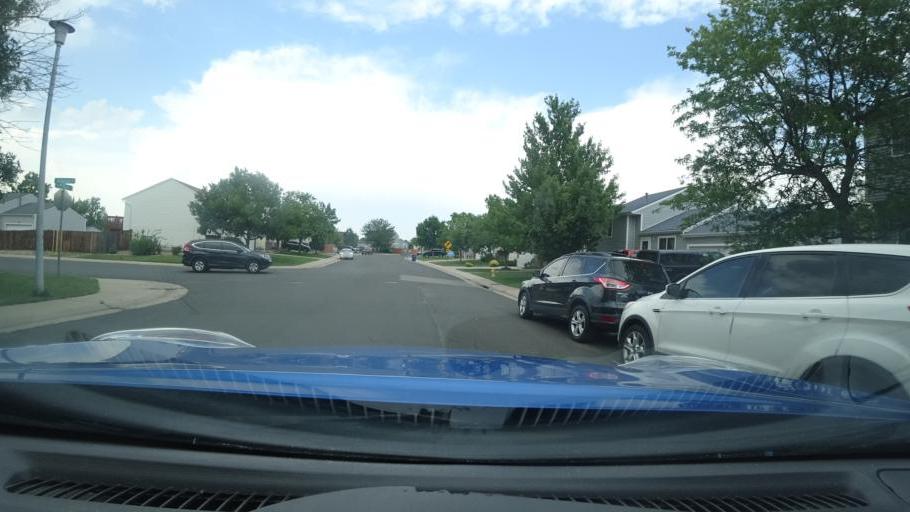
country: US
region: Colorado
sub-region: Adams County
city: Aurora
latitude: 39.6905
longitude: -104.7880
